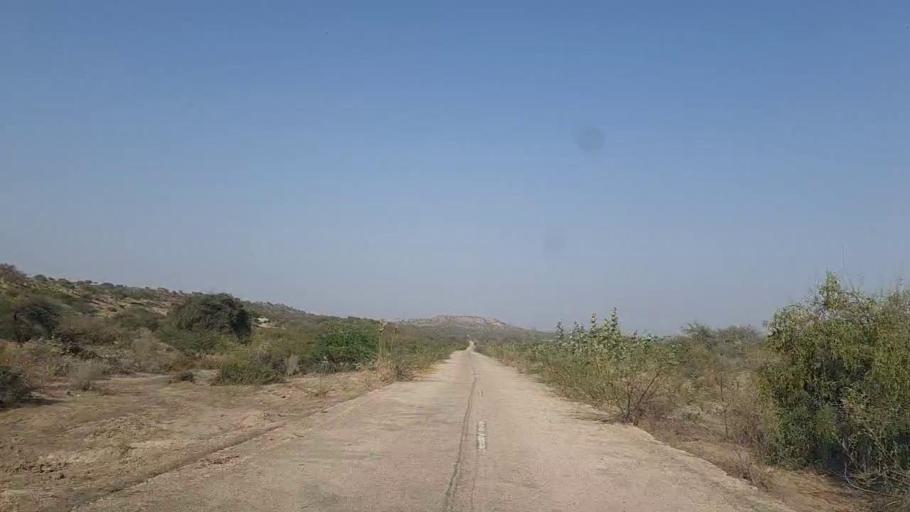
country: PK
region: Sindh
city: Naukot
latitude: 24.6035
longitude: 69.3303
